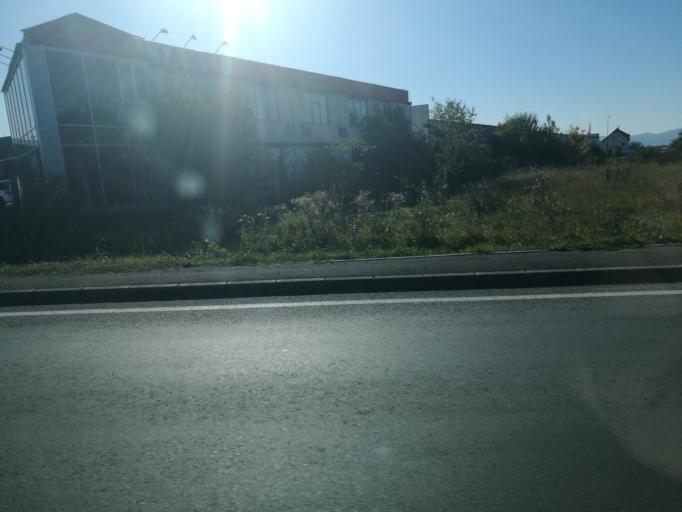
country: RO
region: Brasov
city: Brasov
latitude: 45.6831
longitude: 25.5841
